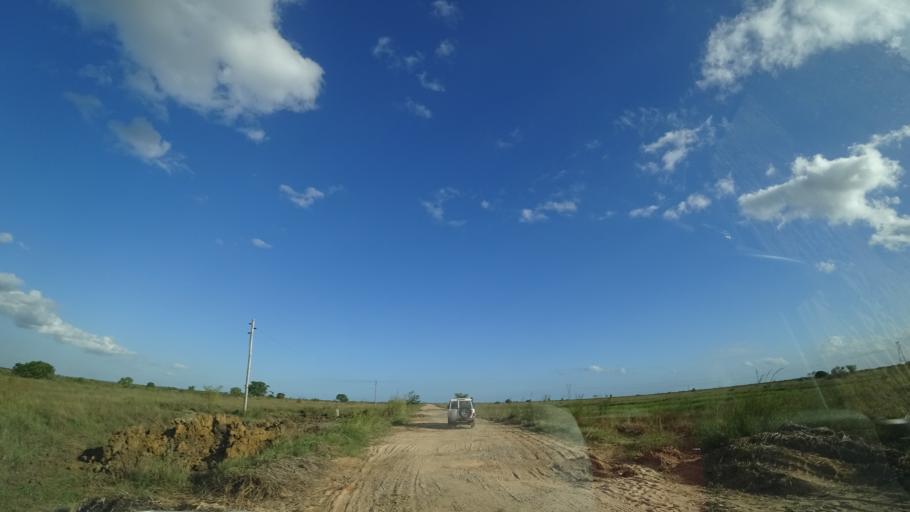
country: MZ
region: Sofala
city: Dondo
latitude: -19.4522
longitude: 34.5627
